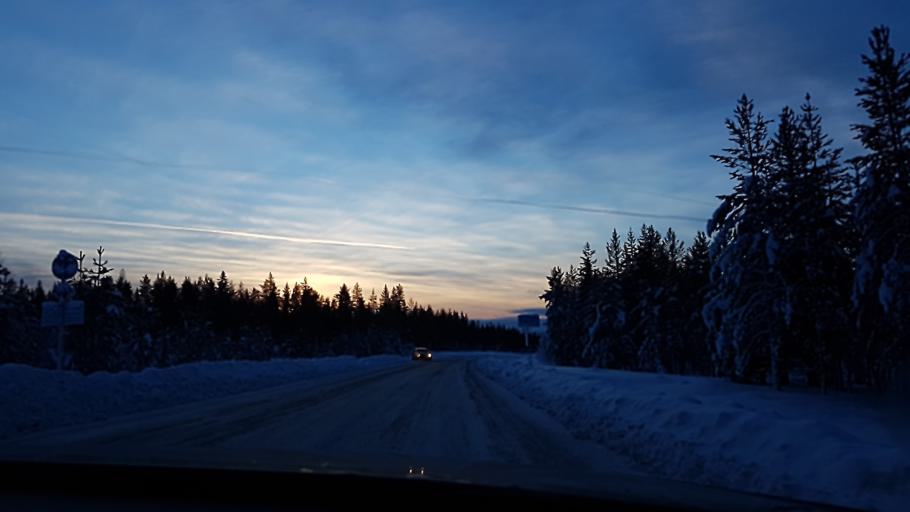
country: SE
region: Norrbotten
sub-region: Jokkmokks Kommun
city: Jokkmokk
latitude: 66.0694
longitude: 20.0773
